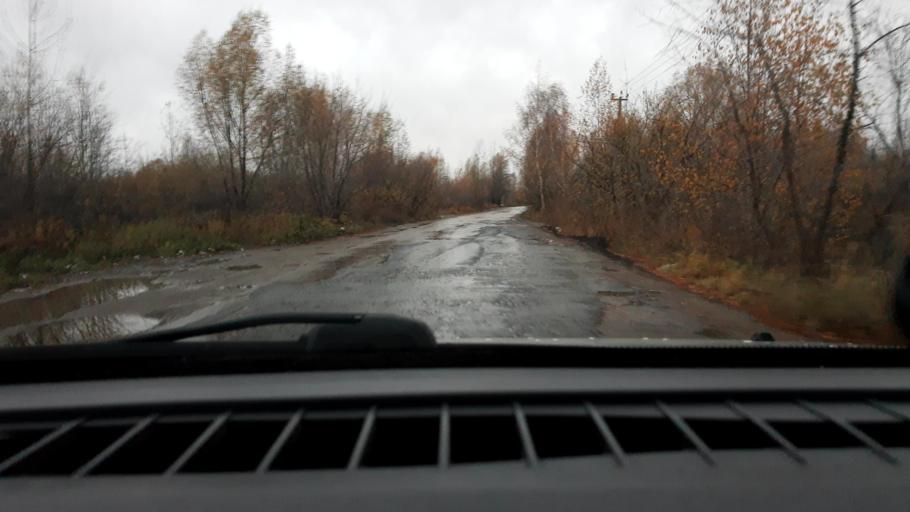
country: RU
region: Nizjnij Novgorod
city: Gorbatovka
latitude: 56.2670
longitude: 43.8587
